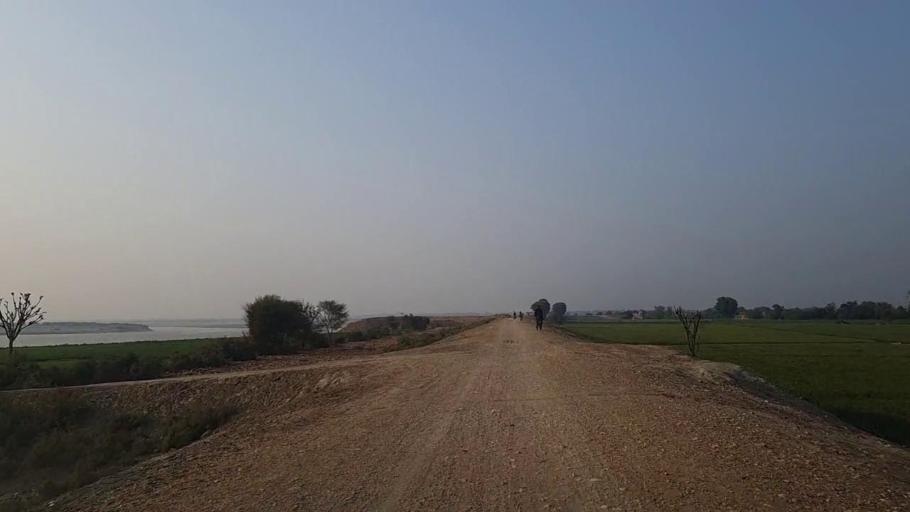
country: PK
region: Sindh
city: Sann
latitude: 26.1304
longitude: 68.1394
